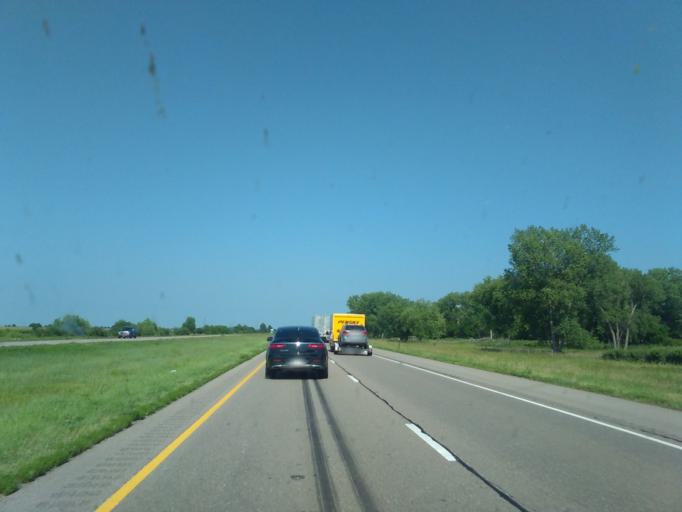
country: US
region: Nebraska
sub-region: Buffalo County
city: Gibbon
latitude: 40.6918
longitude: -98.9032
